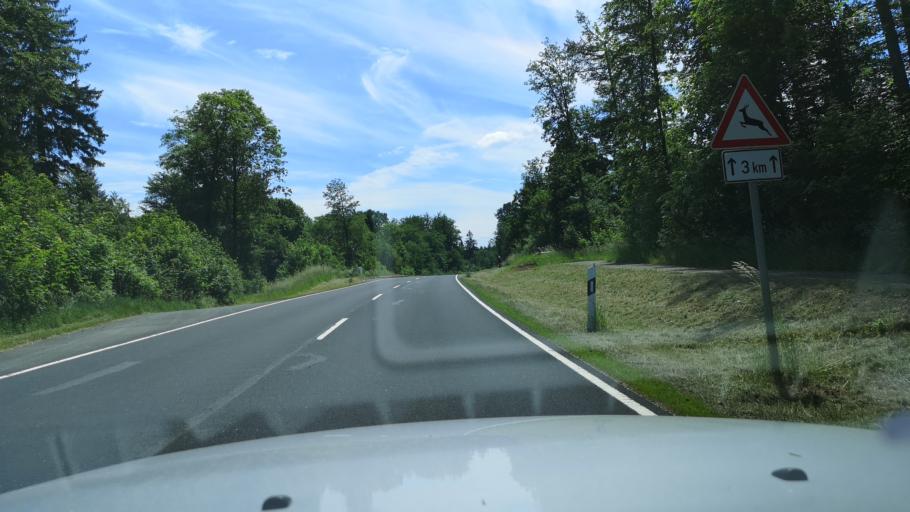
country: DE
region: Bavaria
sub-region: Upper Franconia
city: Ludwigsstadt
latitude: 50.4589
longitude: 11.3449
